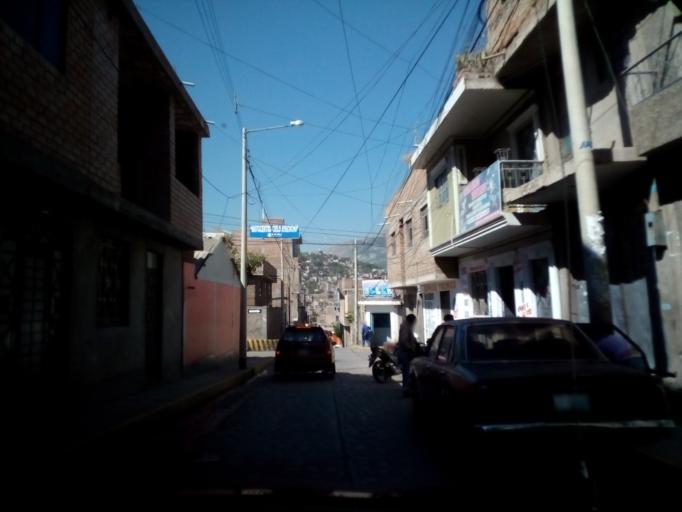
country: PE
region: Ayacucho
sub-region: Provincia de Huamanga
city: Ayacucho
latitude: -13.1590
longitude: -74.2201
